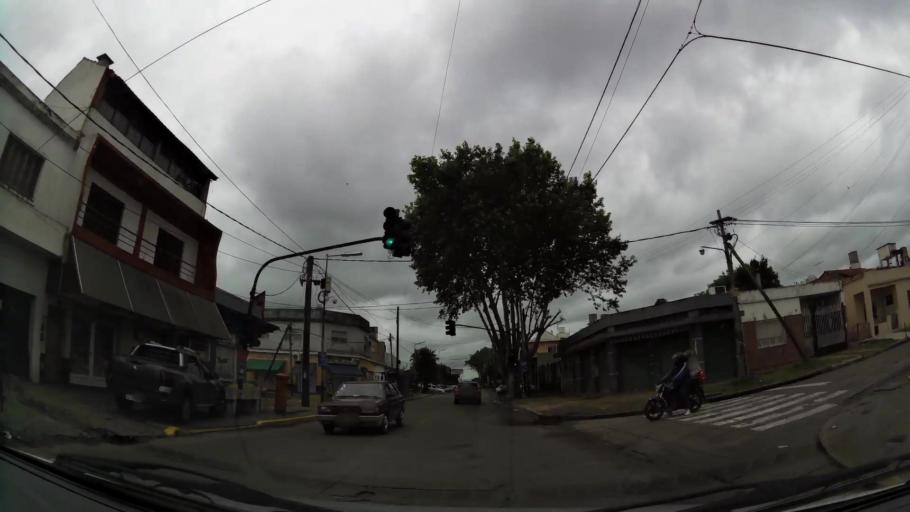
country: AR
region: Buenos Aires
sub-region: Partido de Lomas de Zamora
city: Lomas de Zamora
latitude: -34.7567
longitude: -58.3774
